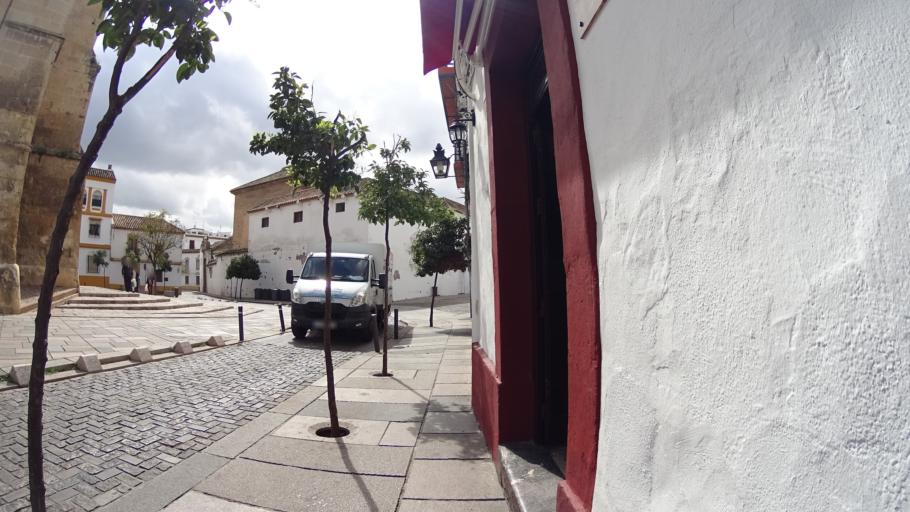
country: ES
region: Andalusia
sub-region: Province of Cordoba
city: Cordoba
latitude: 37.8900
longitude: -4.7751
